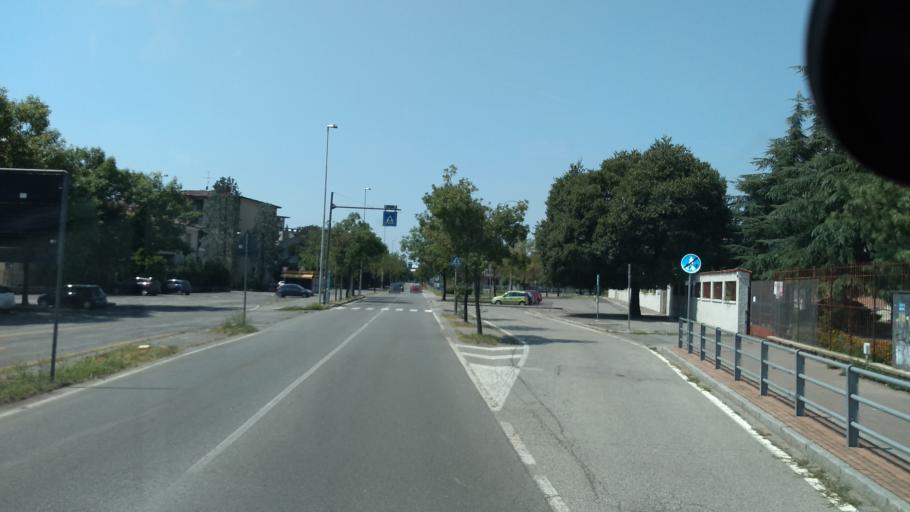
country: IT
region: Lombardy
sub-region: Provincia di Bergamo
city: Treviglio
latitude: 45.5194
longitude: 9.6061
